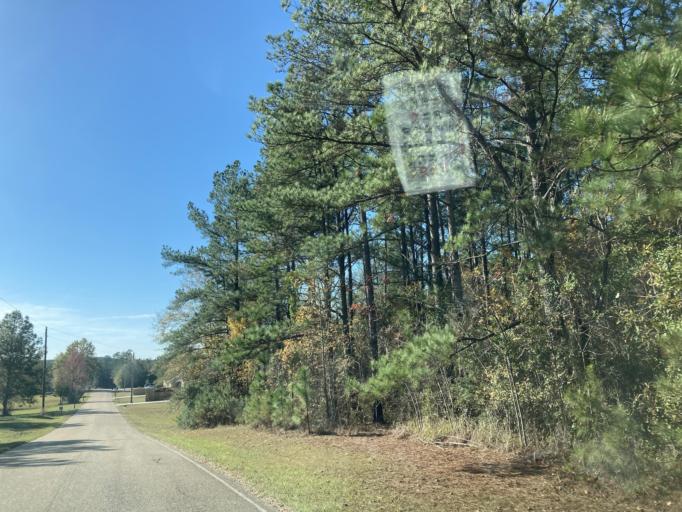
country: US
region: Mississippi
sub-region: Lamar County
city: Sumrall
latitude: 31.2619
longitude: -89.5382
